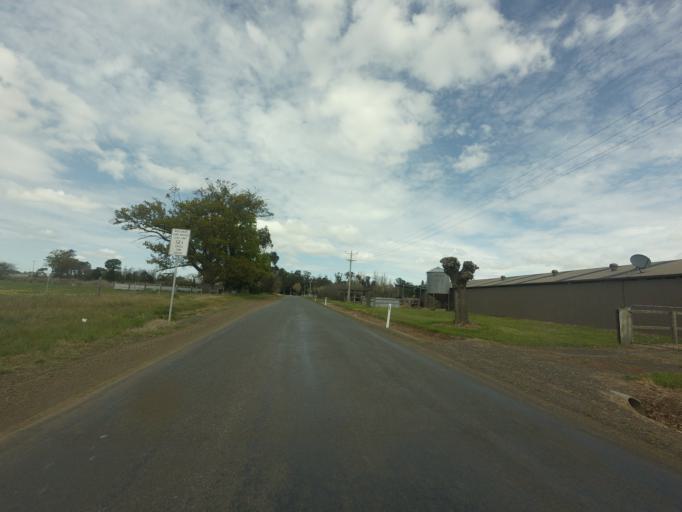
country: AU
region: Tasmania
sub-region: Northern Midlands
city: Longford
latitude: -41.6116
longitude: 147.1281
